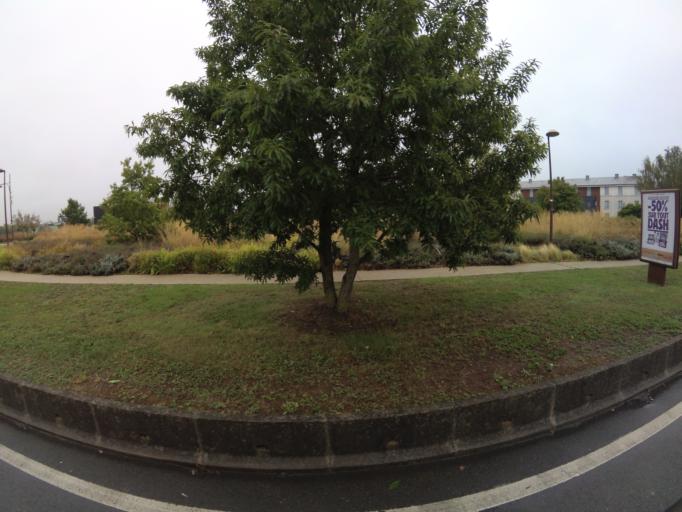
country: FR
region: Ile-de-France
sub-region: Departement de Seine-et-Marne
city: Ferrieres-en-Brie
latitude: 48.8283
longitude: 2.7065
